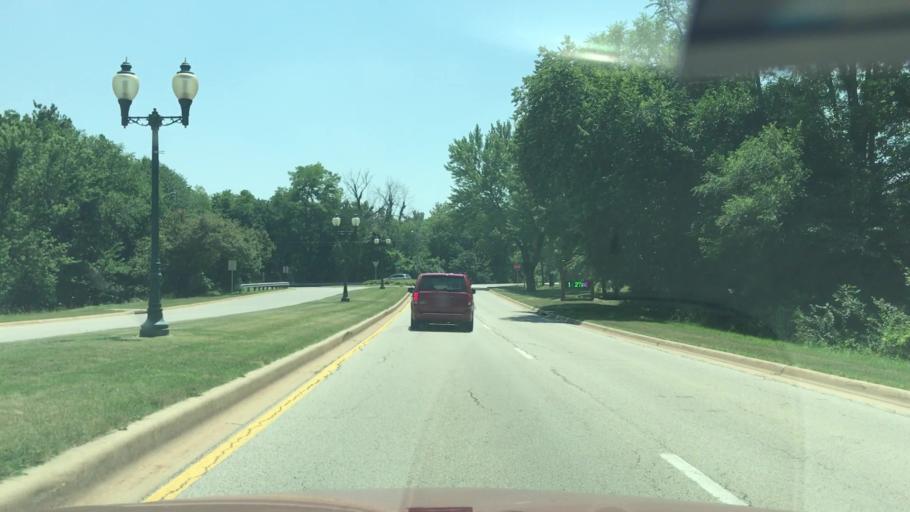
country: US
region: Illinois
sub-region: Winnebago County
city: Cherry Valley
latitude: 42.2375
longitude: -88.9560
